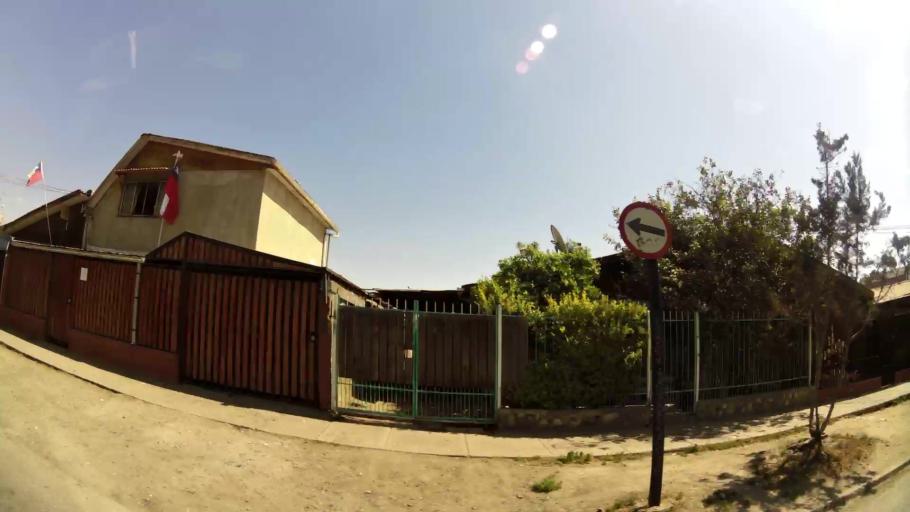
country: CL
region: Santiago Metropolitan
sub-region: Provincia de Santiago
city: La Pintana
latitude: -33.5436
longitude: -70.6449
